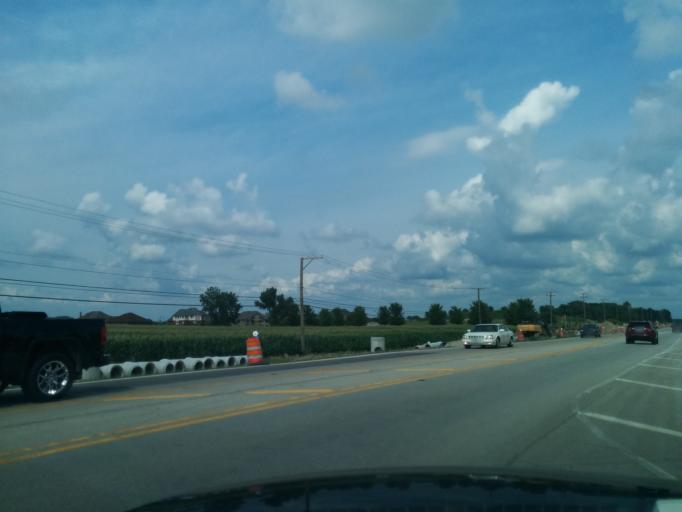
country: US
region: Illinois
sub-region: Will County
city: Homer Glen
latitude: 41.5990
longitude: -87.9710
